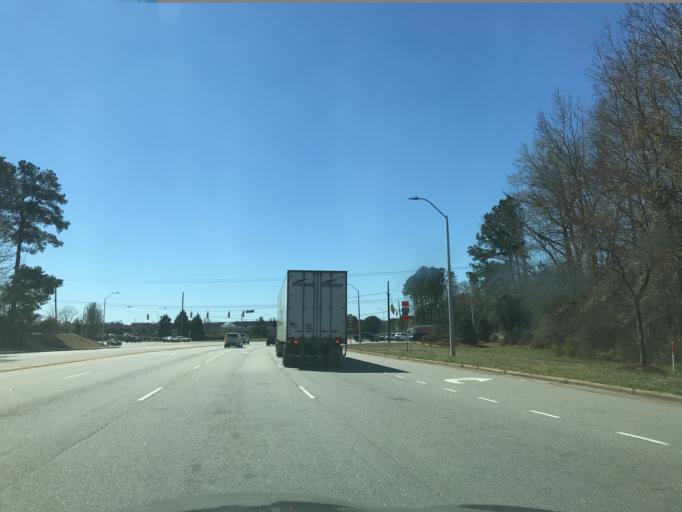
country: US
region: North Carolina
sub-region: Wake County
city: Garner
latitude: 35.7203
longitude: -78.6384
